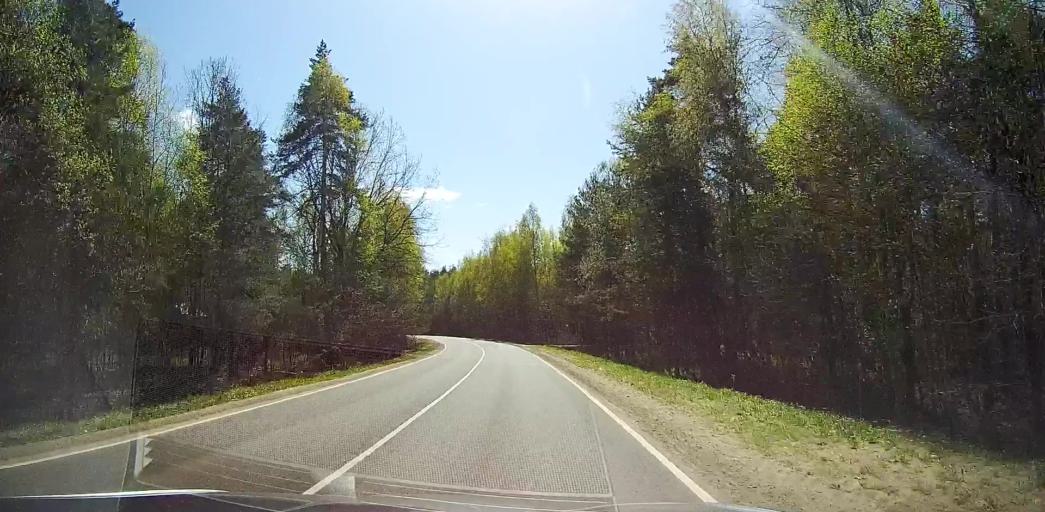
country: RU
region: Moskovskaya
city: Beloozerskiy
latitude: 55.4916
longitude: 38.4272
